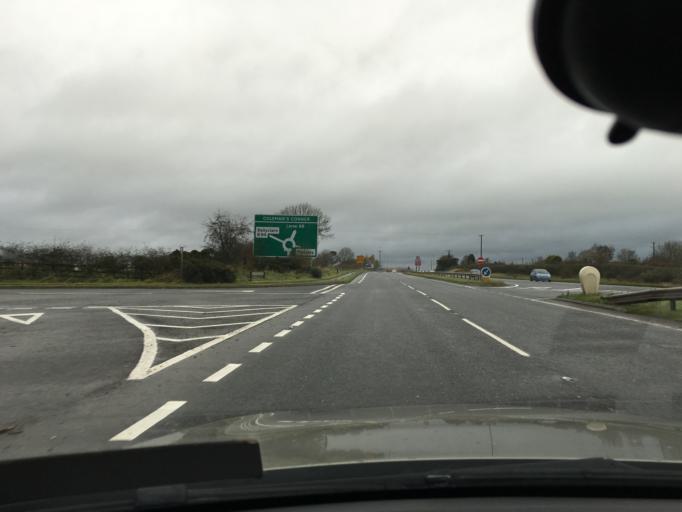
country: GB
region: Northern Ireland
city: Carnmoney
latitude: 54.7211
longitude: -5.9687
